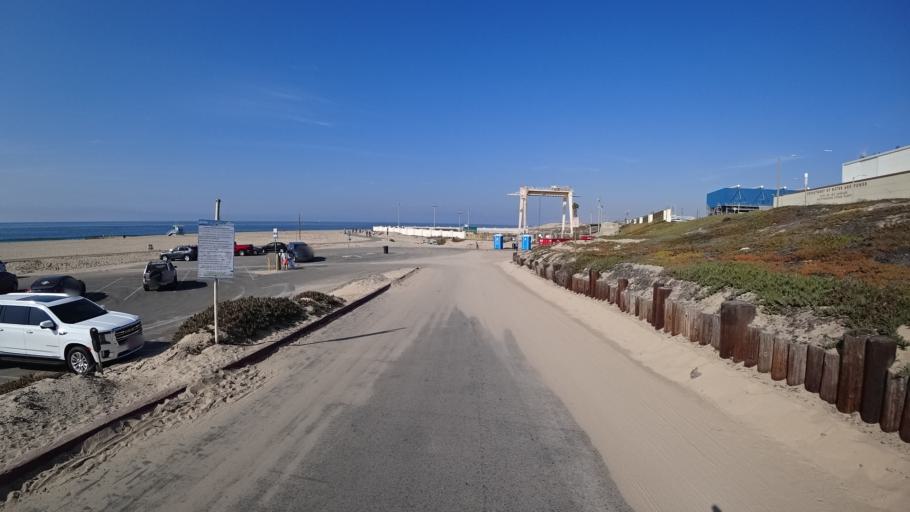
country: US
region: California
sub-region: Los Angeles County
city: El Segundo
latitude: 33.9170
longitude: -118.4284
